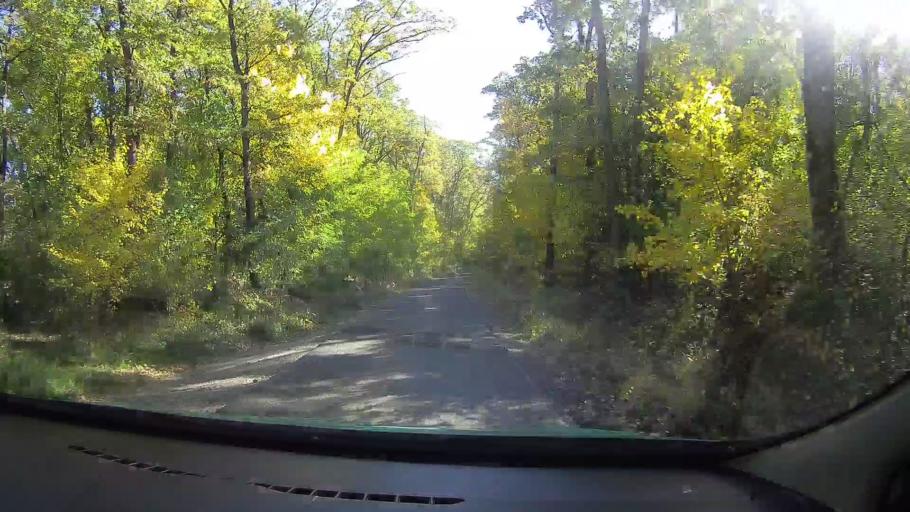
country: RO
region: Satu Mare
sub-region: Comuna Doba
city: Doba
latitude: 47.7162
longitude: 22.7433
